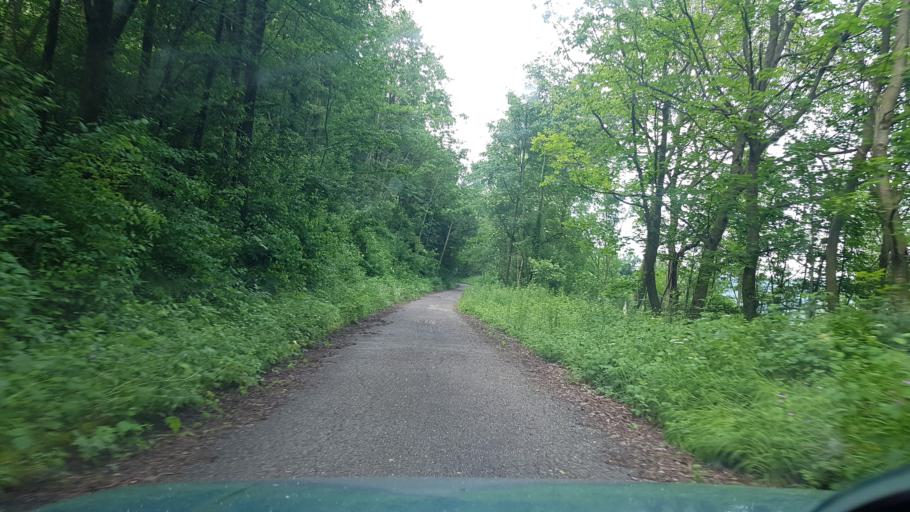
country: IT
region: Friuli Venezia Giulia
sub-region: Provincia di Udine
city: Pulfero
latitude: 46.1709
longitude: 13.4396
